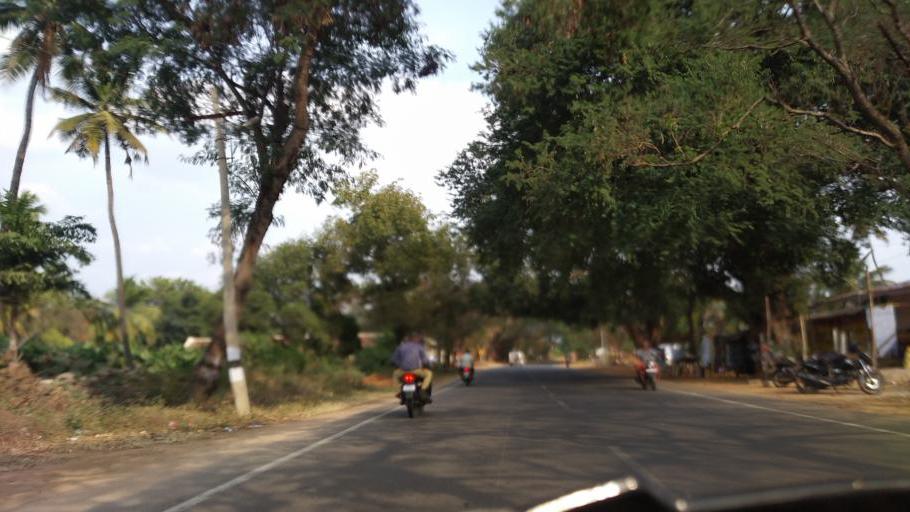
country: IN
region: Tamil Nadu
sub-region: Coimbatore
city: Perur
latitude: 10.9720
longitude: 76.8823
